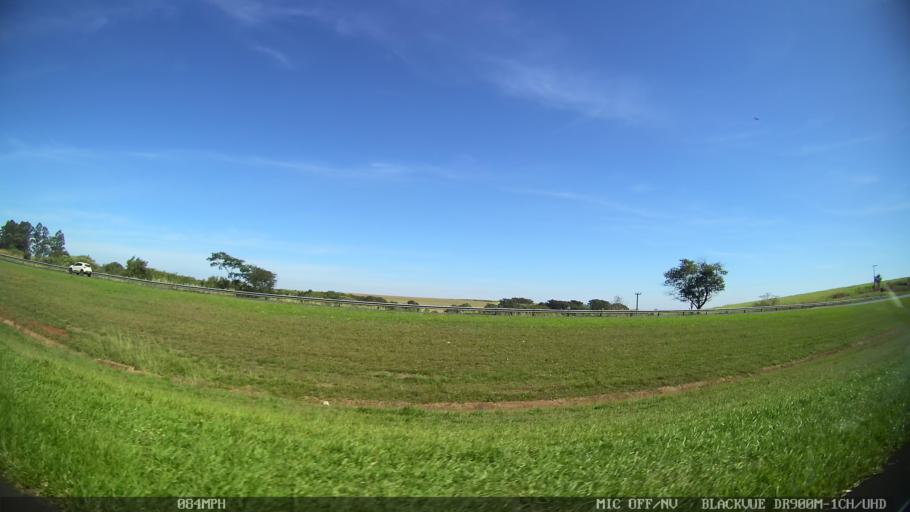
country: BR
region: Sao Paulo
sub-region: Santa Rita Do Passa Quatro
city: Santa Rita do Passa Quatro
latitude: -21.6752
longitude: -47.6052
